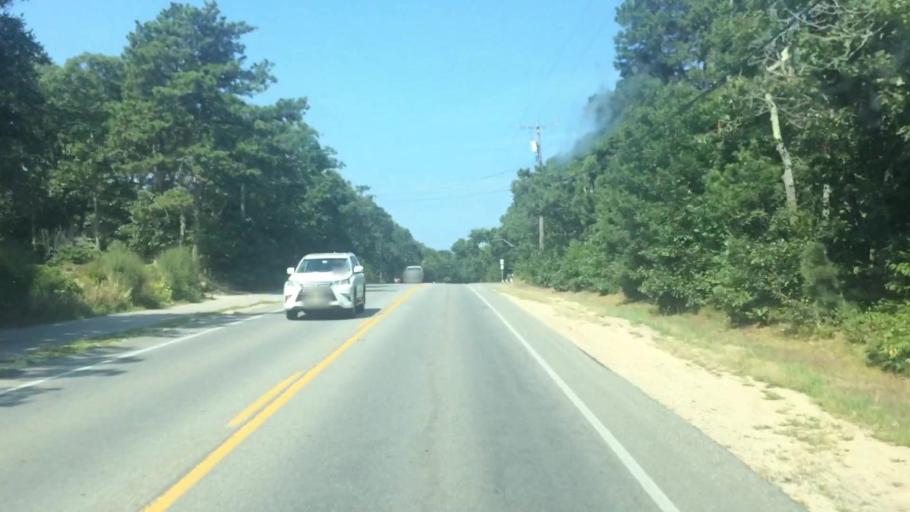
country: US
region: Massachusetts
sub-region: Dukes County
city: Edgartown
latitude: 41.3982
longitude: -70.5421
